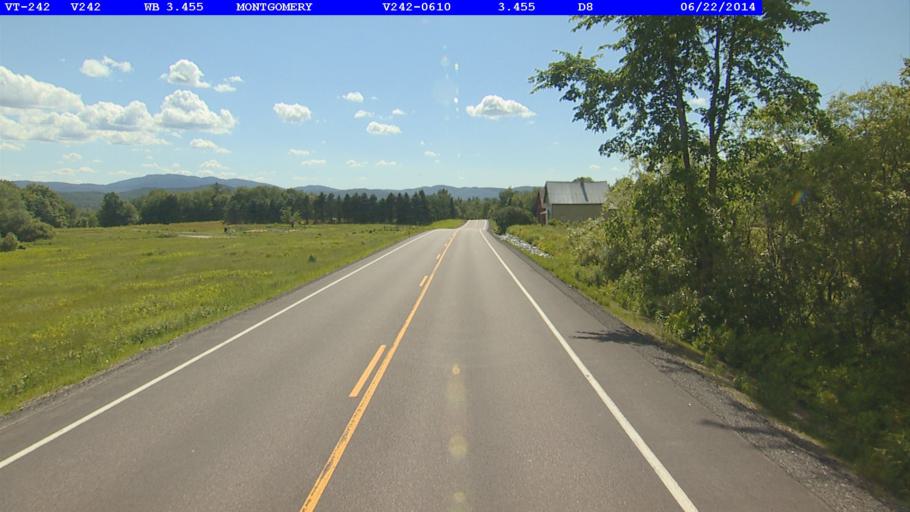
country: US
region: Vermont
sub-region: Franklin County
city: Richford
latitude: 44.8836
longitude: -72.5442
